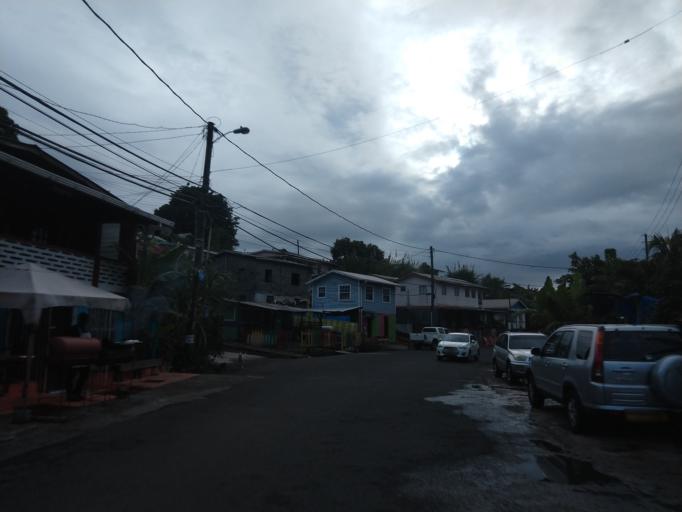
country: GD
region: Saint George
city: Saint George's
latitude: 12.0576
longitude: -61.7523
